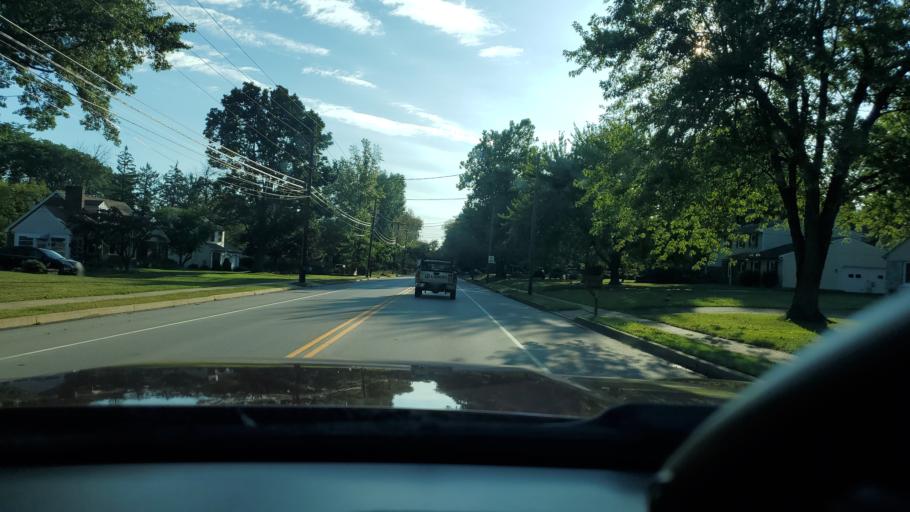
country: US
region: Pennsylvania
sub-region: Montgomery County
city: Telford
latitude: 40.3140
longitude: -75.3450
